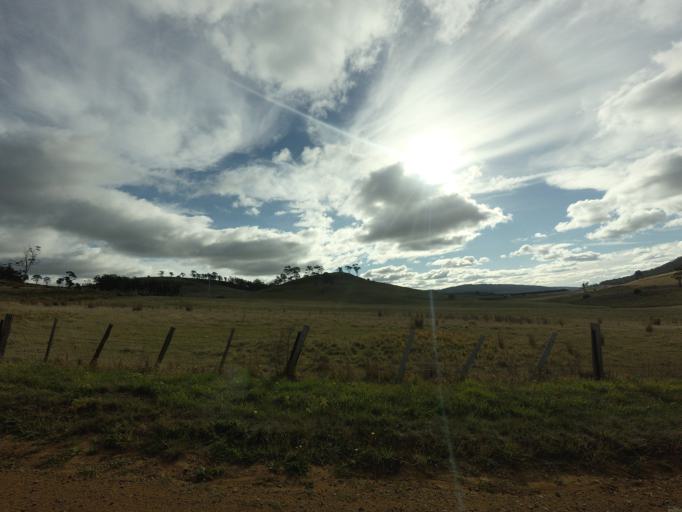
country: AU
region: Tasmania
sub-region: Brighton
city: Bridgewater
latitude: -42.4904
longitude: 147.3303
